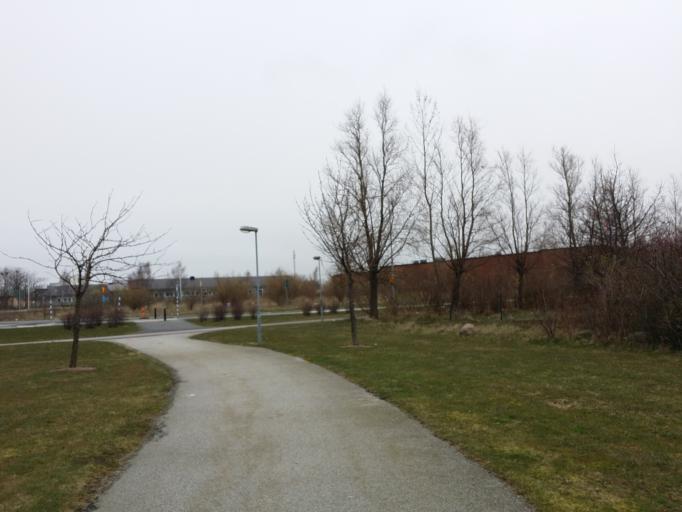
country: SE
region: Skane
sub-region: Burlovs Kommun
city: Arloev
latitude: 55.6098
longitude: 13.0841
